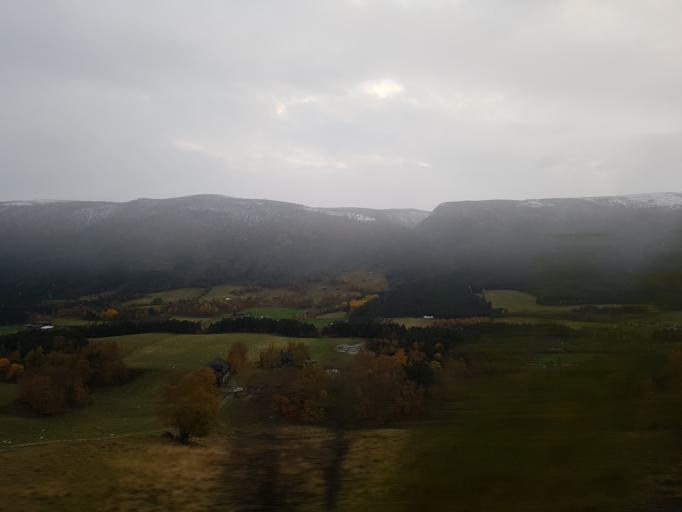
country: NO
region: Oppland
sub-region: Dovre
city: Dovre
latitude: 62.0227
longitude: 9.1885
